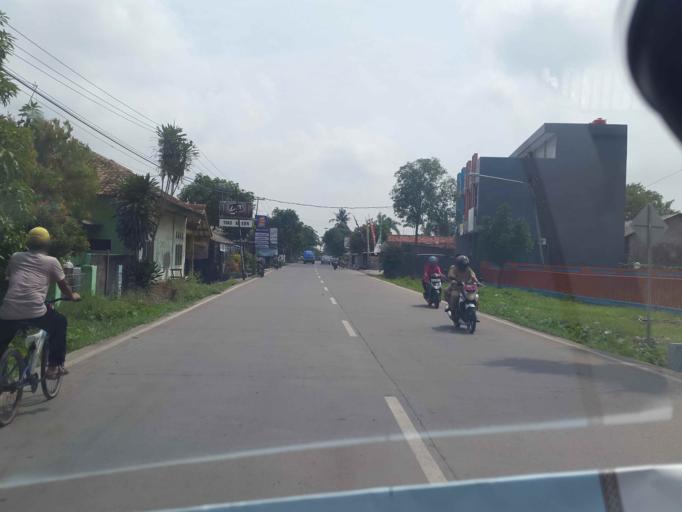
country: ID
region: West Java
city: Rengasdengklok
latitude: -6.2946
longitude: 107.3346
